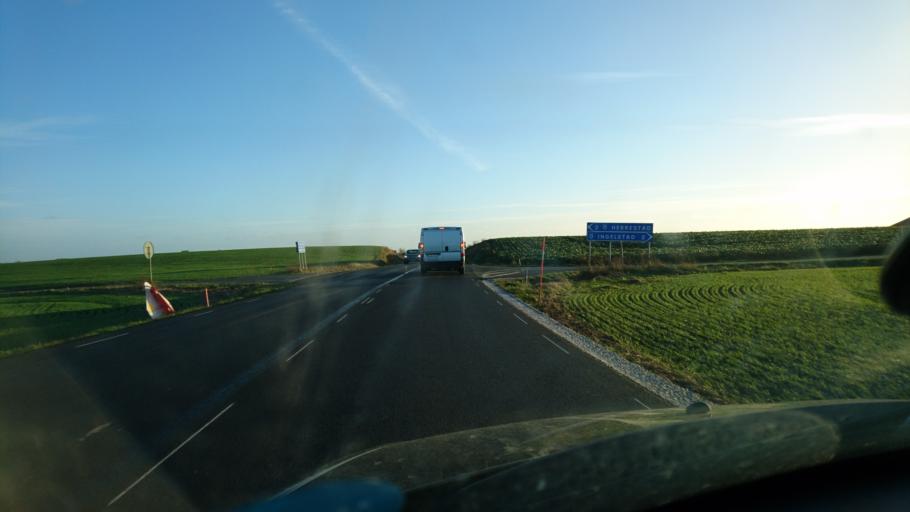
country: SE
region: Skane
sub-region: Tomelilla Kommun
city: Tomelilla
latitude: 55.5258
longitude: 14.1269
